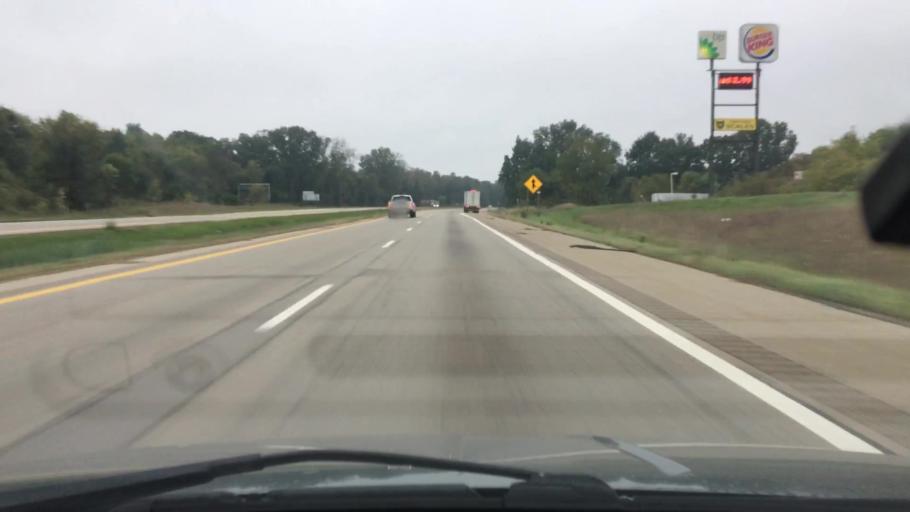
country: US
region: Michigan
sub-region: Jackson County
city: Concord
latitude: 42.2653
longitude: -84.6220
